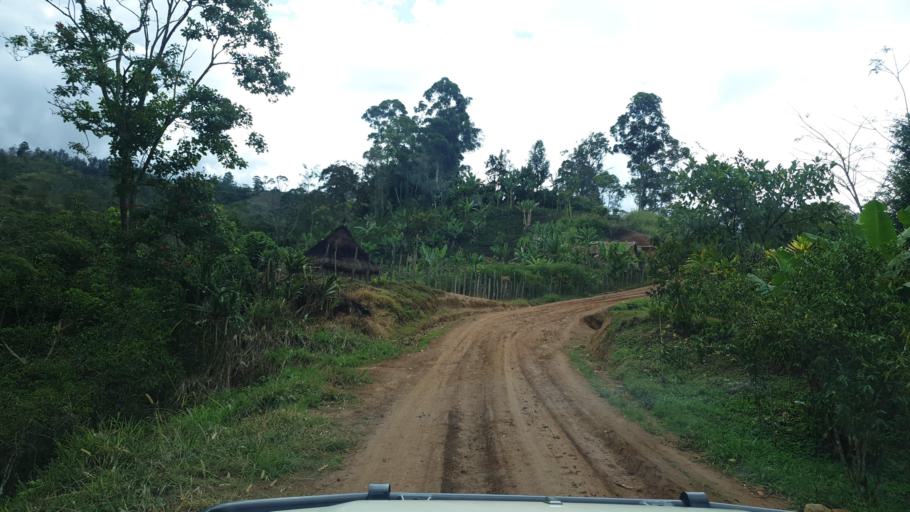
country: PG
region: Eastern Highlands
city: Goroka
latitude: -5.9335
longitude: 145.2644
